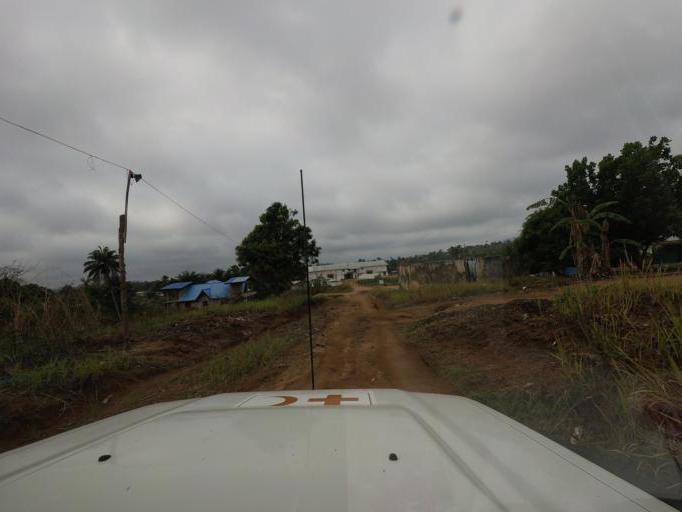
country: LR
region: Lofa
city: Voinjama
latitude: 8.4284
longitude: -9.7564
